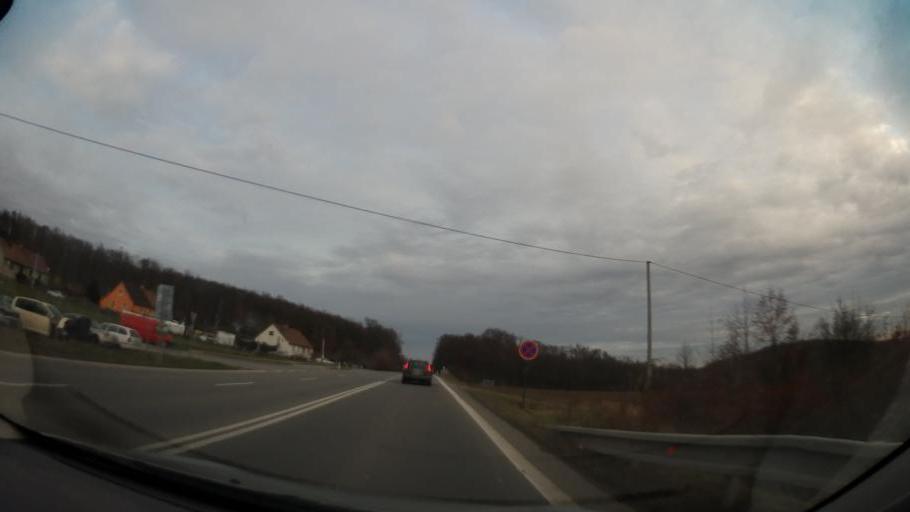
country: CZ
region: South Moravian
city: Ricany
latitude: 49.1908
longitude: 16.4443
